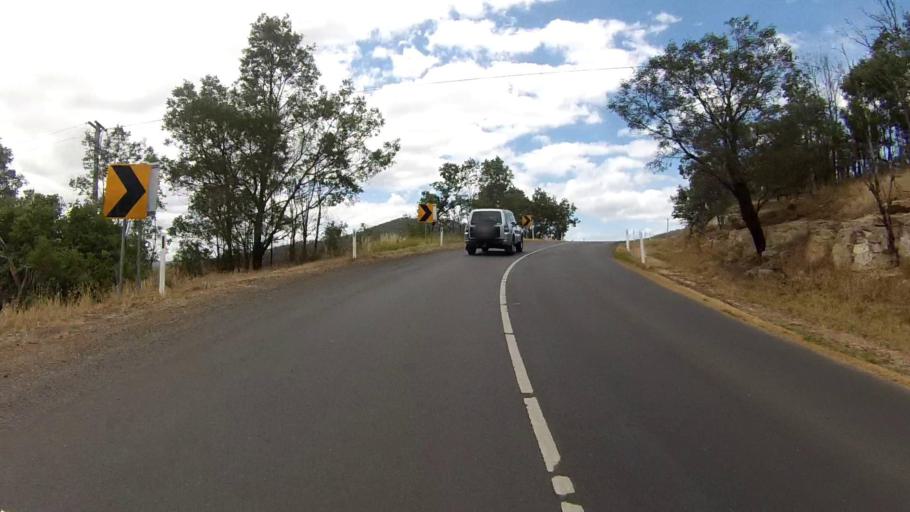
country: AU
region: Tasmania
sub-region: Sorell
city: Sorell
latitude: -42.8085
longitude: 147.6121
